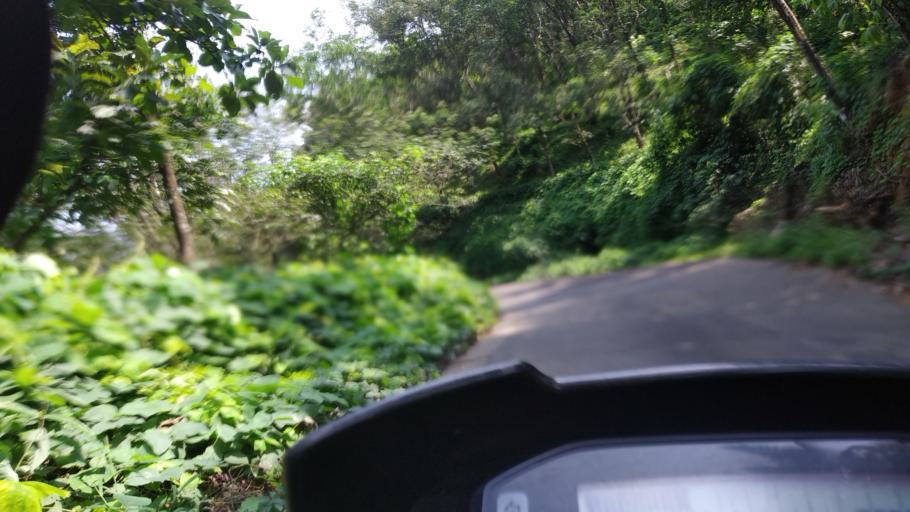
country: IN
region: Kerala
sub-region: Kottayam
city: Erattupetta
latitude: 9.6937
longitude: 76.8707
